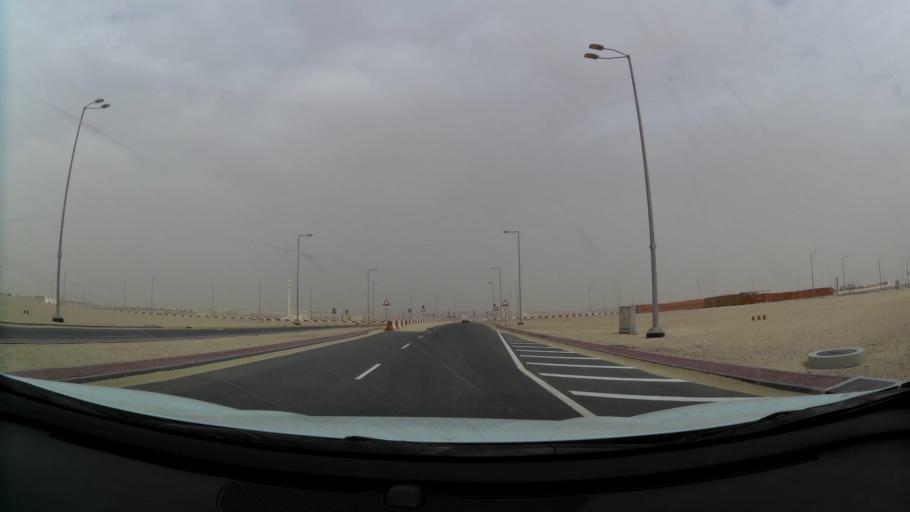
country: AE
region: Abu Dhabi
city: Abu Dhabi
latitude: 24.3623
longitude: 54.7413
